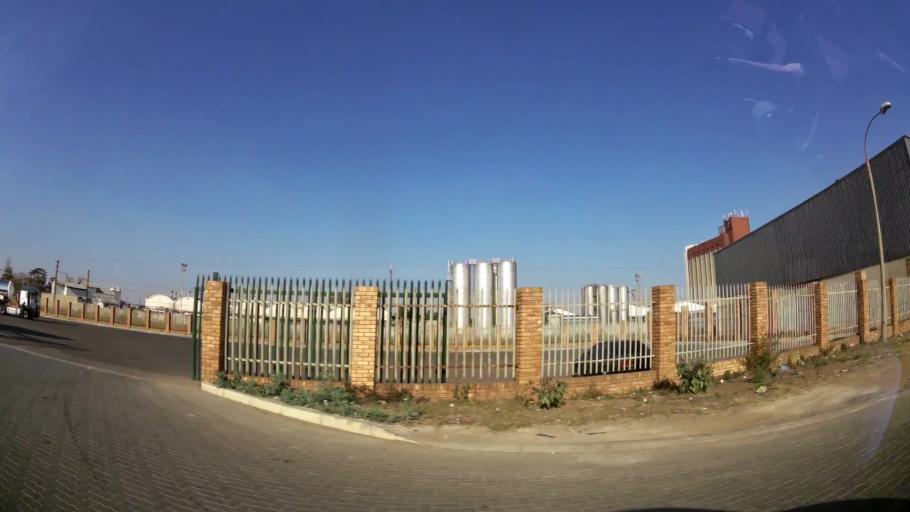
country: ZA
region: Gauteng
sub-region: West Rand District Municipality
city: Randfontein
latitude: -26.1617
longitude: 27.7114
